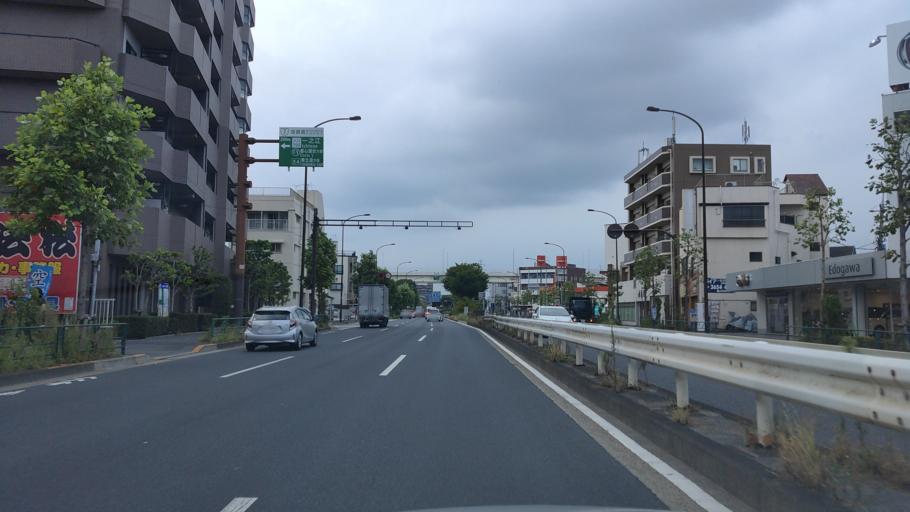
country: JP
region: Tokyo
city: Urayasu
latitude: 35.6948
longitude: 139.8824
